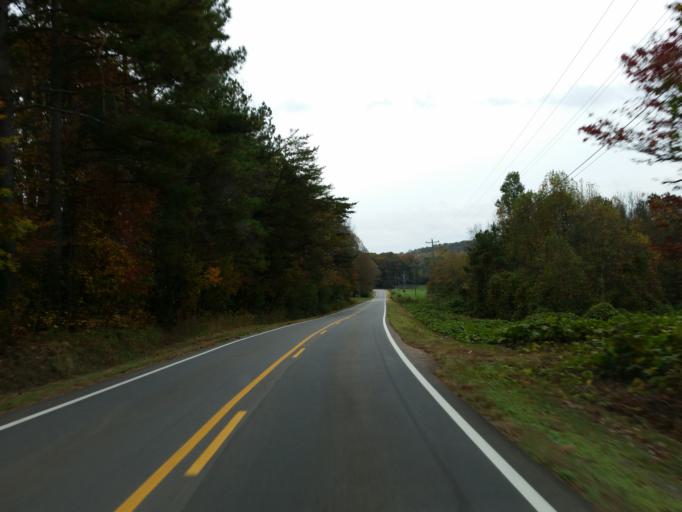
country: US
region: Georgia
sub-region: Gilmer County
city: Ellijay
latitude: 34.6592
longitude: -84.3618
